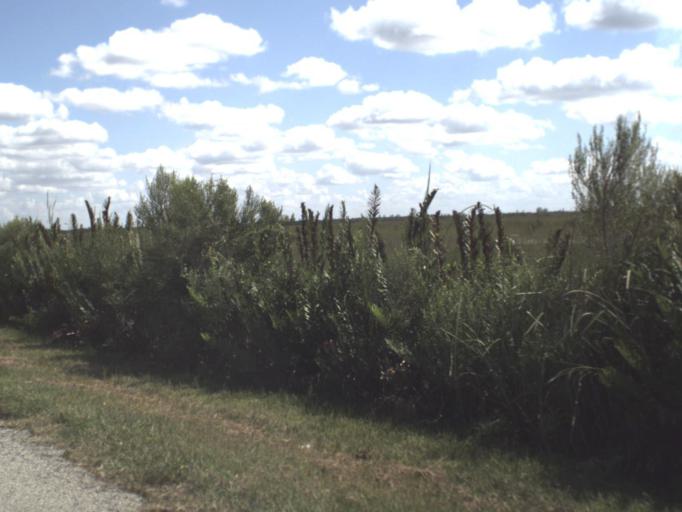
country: US
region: Florida
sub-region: Collier County
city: Marco
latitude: 25.9183
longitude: -81.3880
